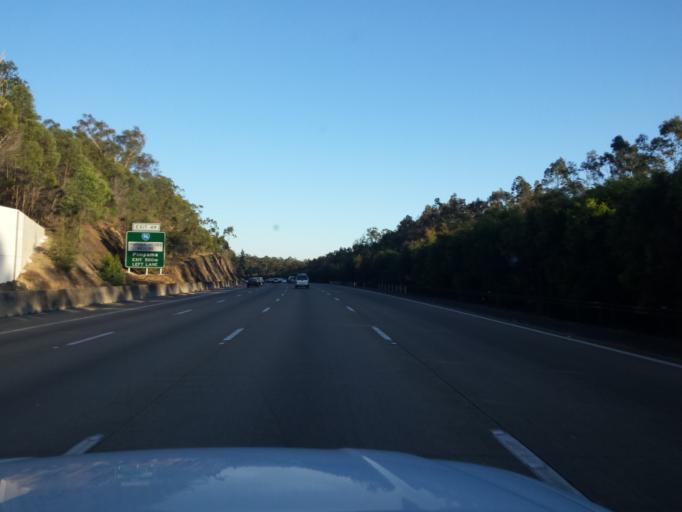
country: AU
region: Queensland
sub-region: Gold Coast
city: Ormeau Hills
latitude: -27.8261
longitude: 153.2976
